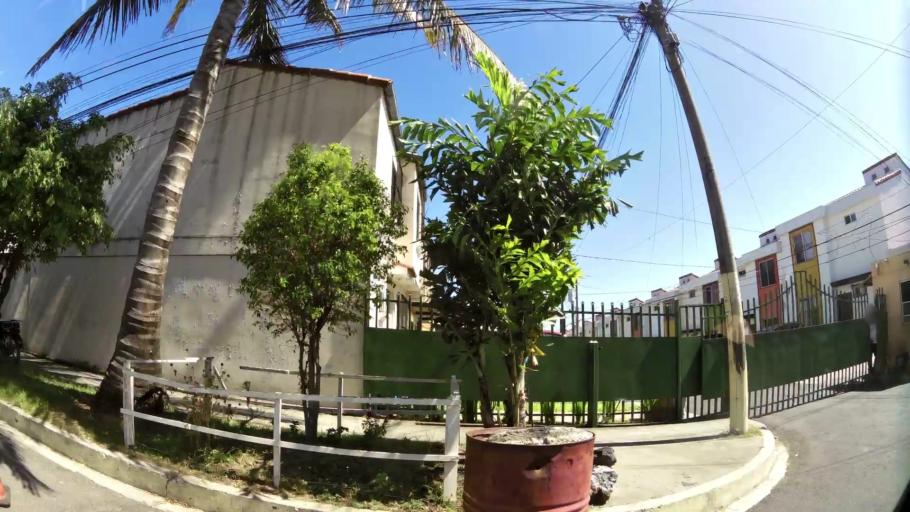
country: SV
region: La Libertad
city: Santa Tecla
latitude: 13.6682
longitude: -89.2764
